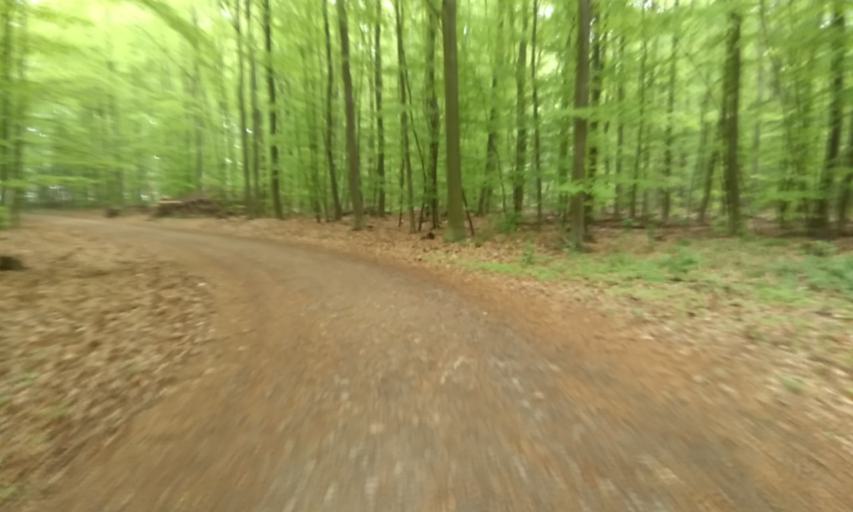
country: DE
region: Lower Saxony
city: Nottensdorf
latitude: 53.4770
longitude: 9.6196
